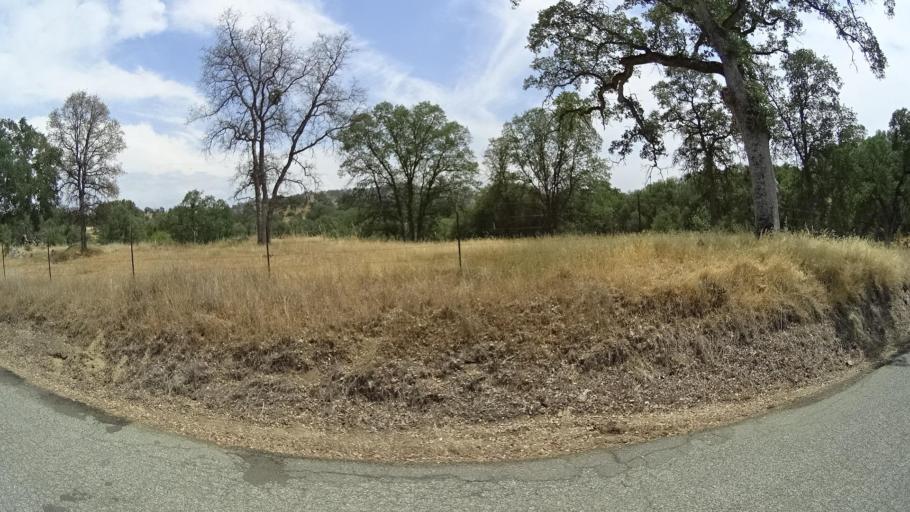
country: US
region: California
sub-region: Mariposa County
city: Mariposa
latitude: 37.3820
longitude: -119.8728
